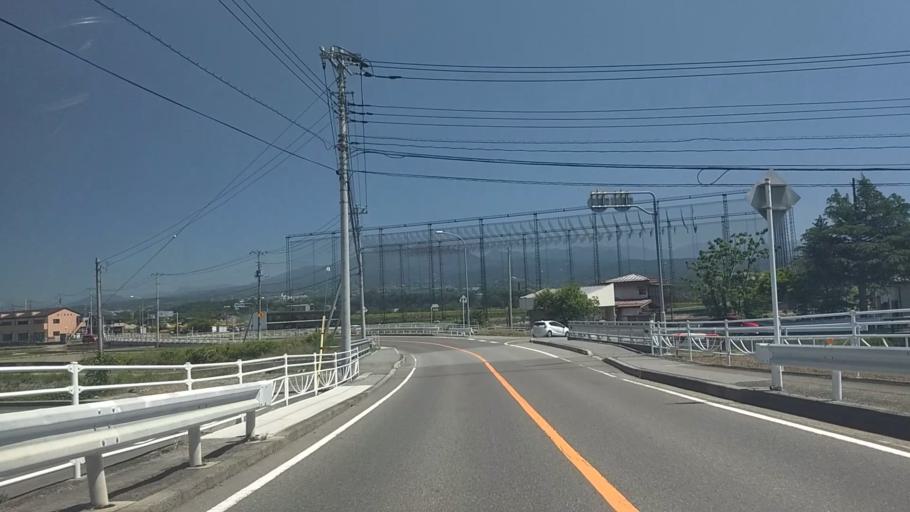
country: JP
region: Yamanashi
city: Nirasaki
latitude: 35.6868
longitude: 138.4616
